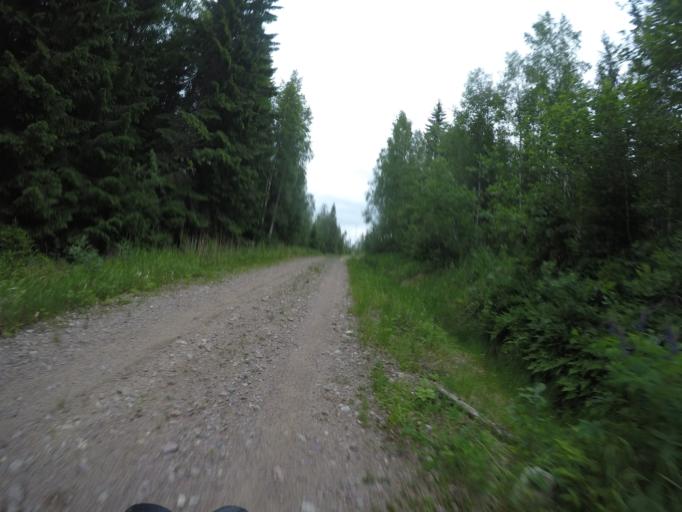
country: SE
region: Dalarna
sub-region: Ludvika Kommun
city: Abborrberget
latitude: 60.0363
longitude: 14.5966
